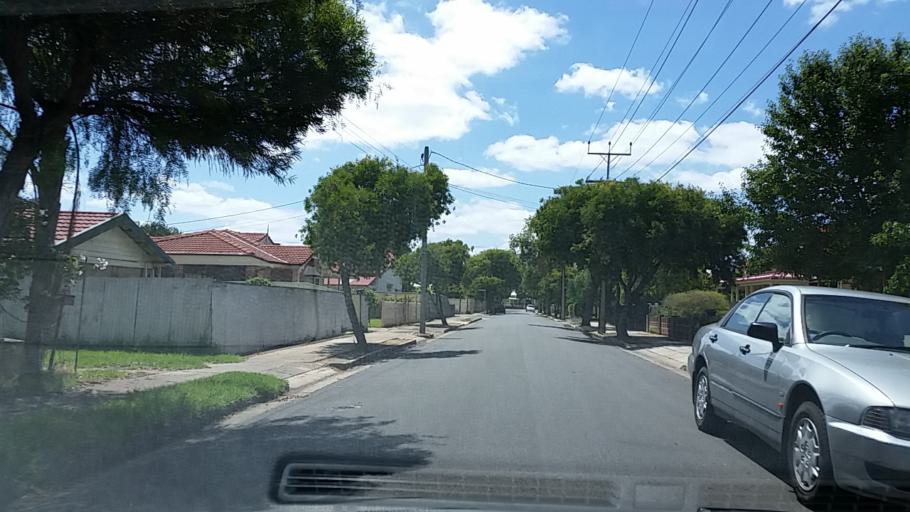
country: AU
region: South Australia
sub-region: City of West Torrens
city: Thebarton
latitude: -34.9263
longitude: 138.5566
